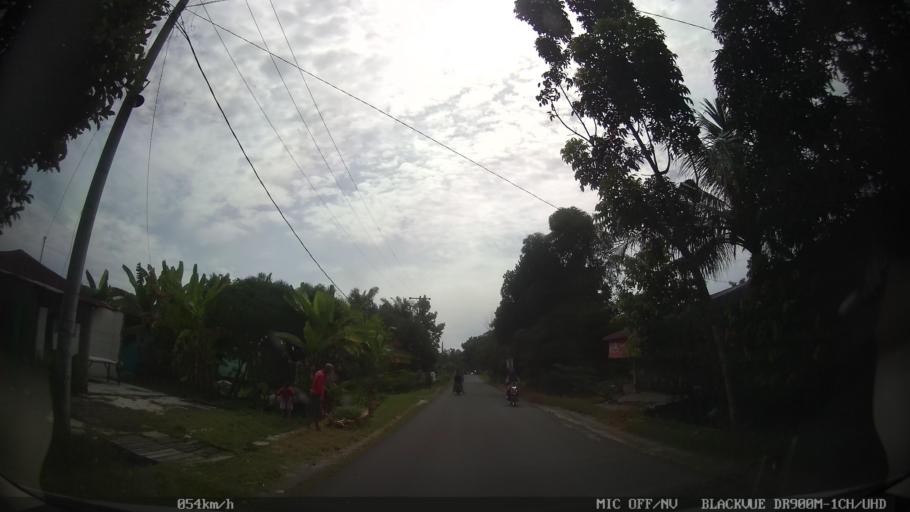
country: ID
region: North Sumatra
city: Percut
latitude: 3.6199
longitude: 98.7870
